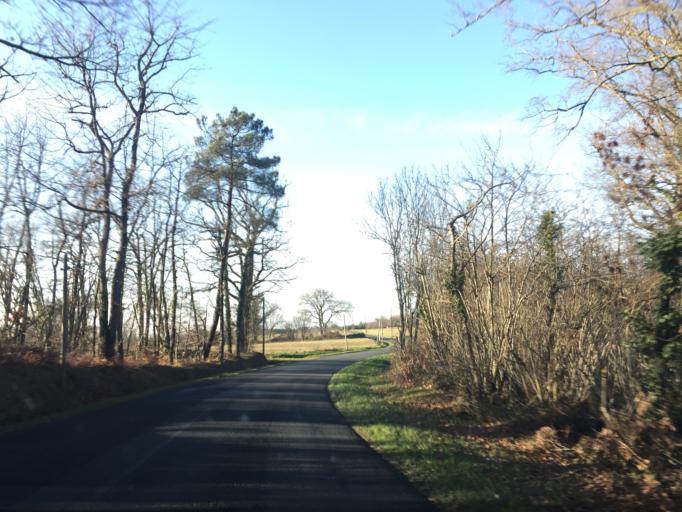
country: FR
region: Aquitaine
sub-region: Departement de la Dordogne
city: Riberac
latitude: 45.2109
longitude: 0.3007
